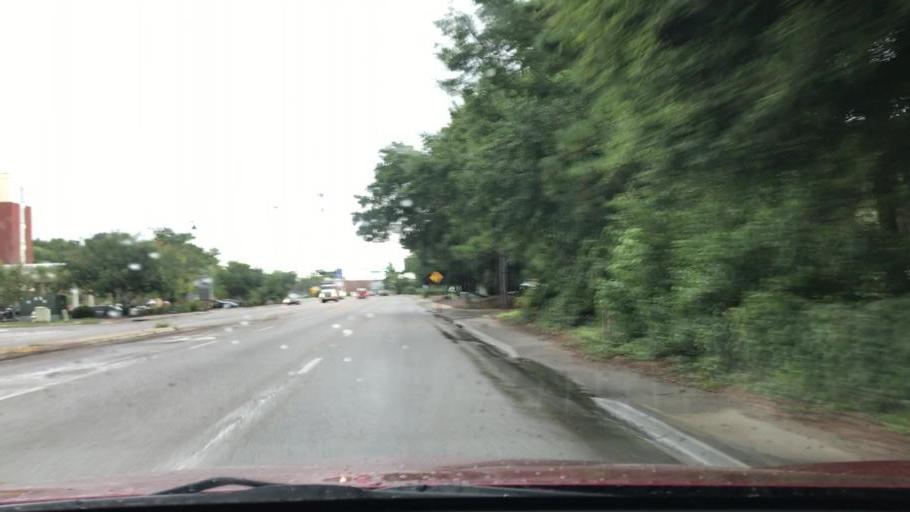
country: US
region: South Carolina
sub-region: Charleston County
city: North Charleston
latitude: 32.8636
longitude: -80.0185
